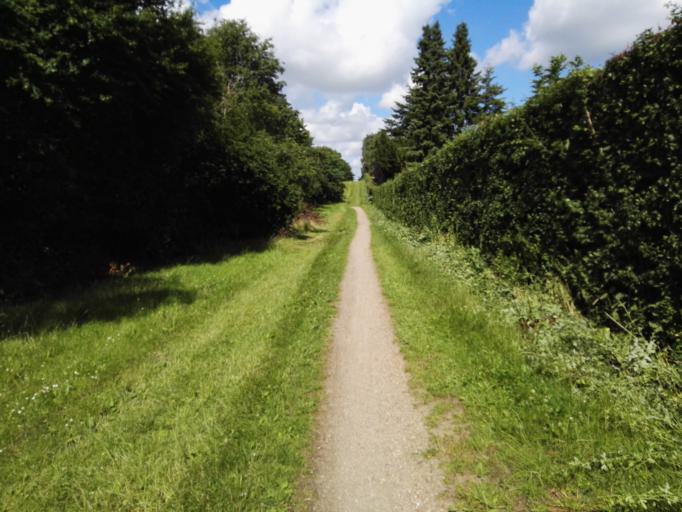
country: DK
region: Capital Region
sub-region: Ballerup Kommune
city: Ballerup
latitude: 55.7352
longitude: 12.3761
